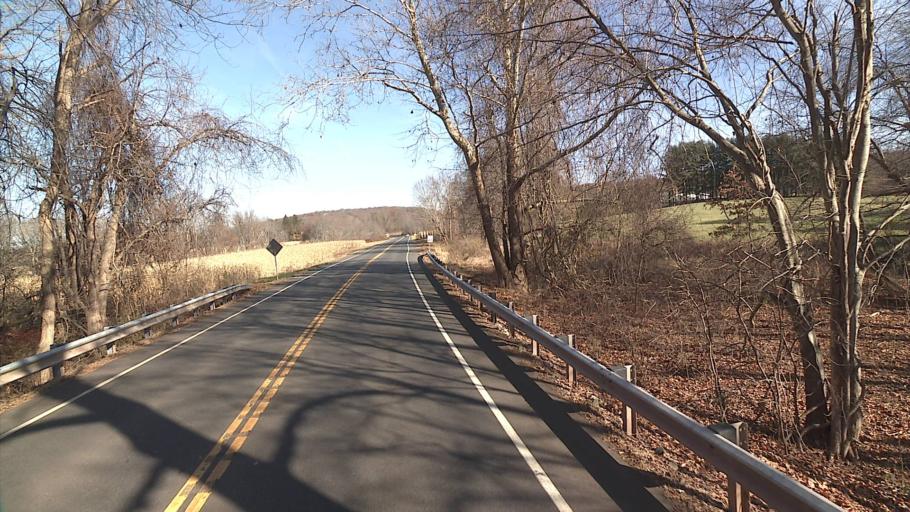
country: US
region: Connecticut
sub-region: Middlesex County
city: Cromwell
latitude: 41.5913
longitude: -72.6101
